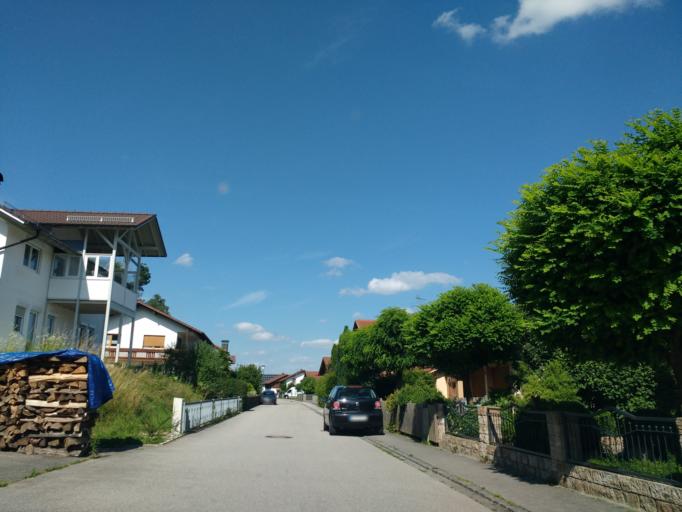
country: DE
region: Bavaria
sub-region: Upper Bavaria
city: Taufkirchen
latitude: 48.1455
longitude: 12.4527
